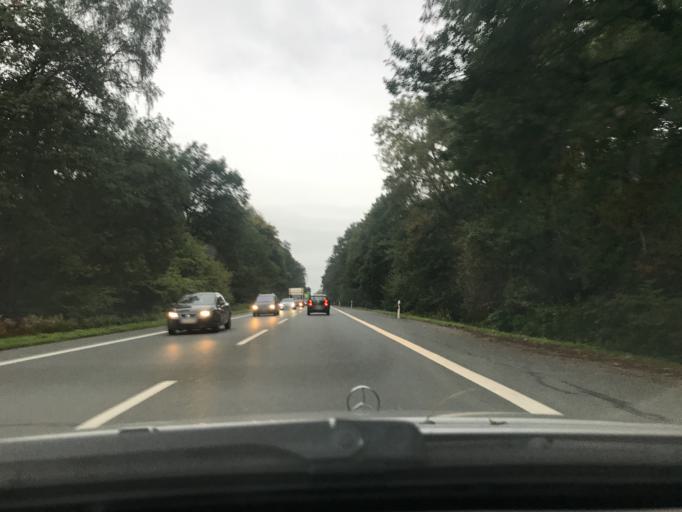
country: DE
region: North Rhine-Westphalia
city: Herten
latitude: 51.5578
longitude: 7.1137
